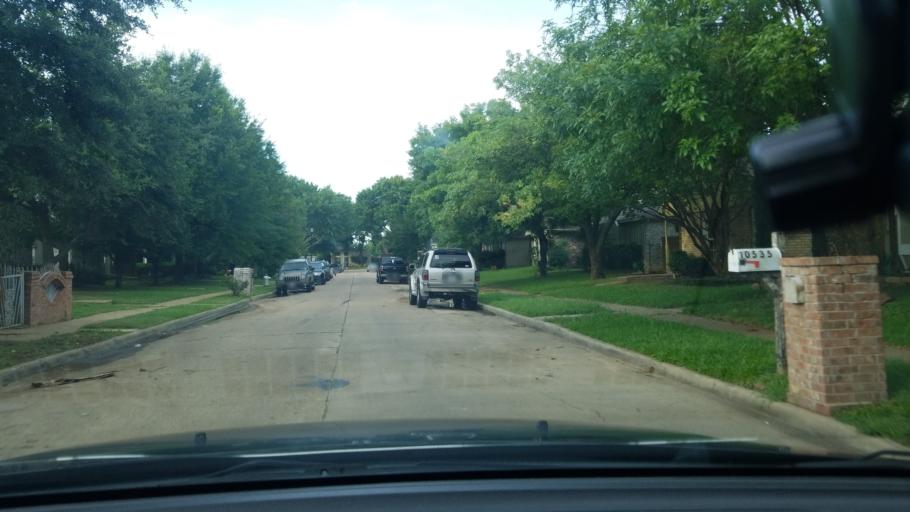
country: US
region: Texas
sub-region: Dallas County
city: Balch Springs
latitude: 32.7528
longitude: -96.6424
